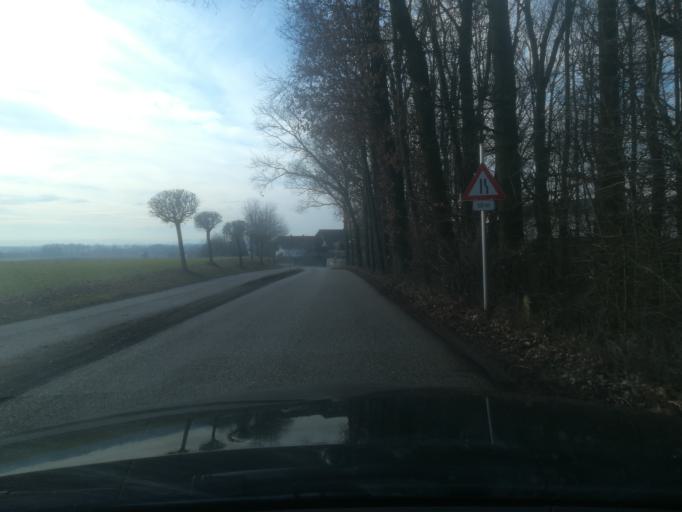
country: AT
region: Upper Austria
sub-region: Wels-Land
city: Holzhausen
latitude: 48.2338
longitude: 14.1219
